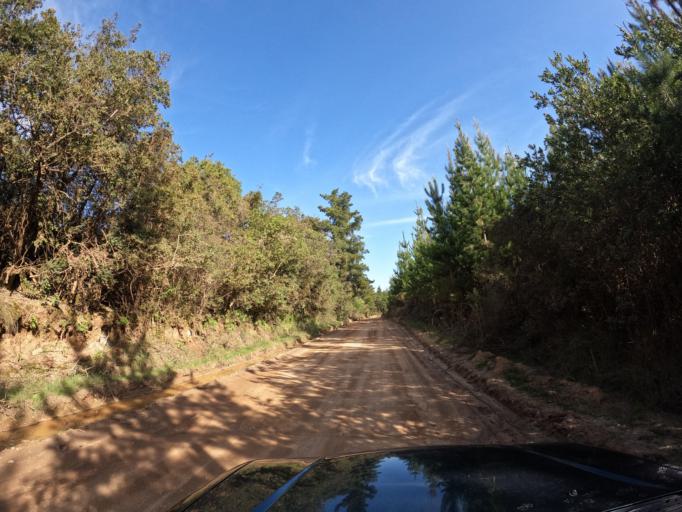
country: CL
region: Biobio
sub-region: Provincia de Biobio
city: La Laja
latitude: -37.1130
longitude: -72.7392
